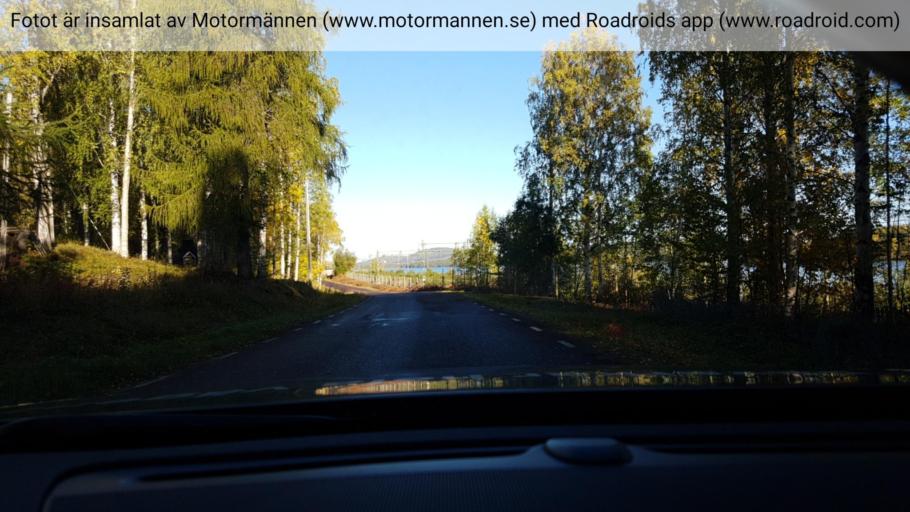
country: SE
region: Norrbotten
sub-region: Bodens Kommun
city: Boden
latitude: 66.1250
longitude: 21.3208
